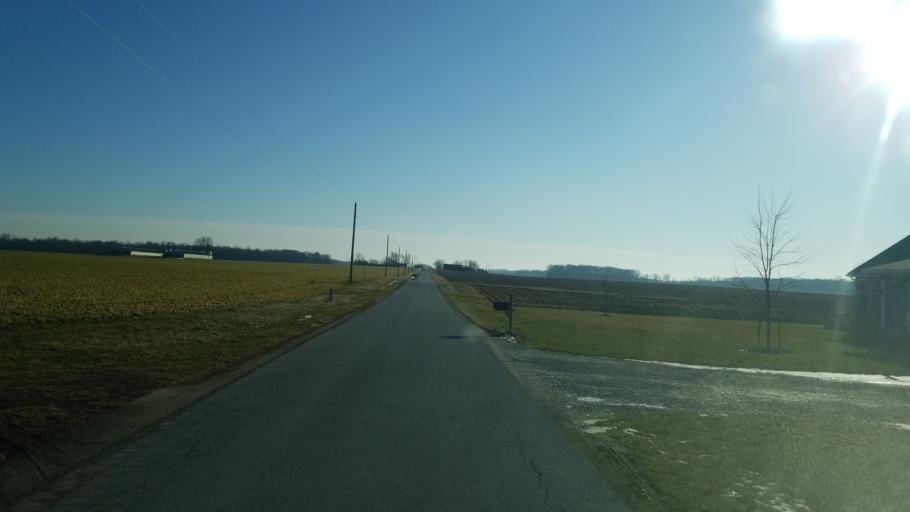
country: US
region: Ohio
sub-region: Sandusky County
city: Green Springs
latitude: 41.1897
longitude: -82.9953
